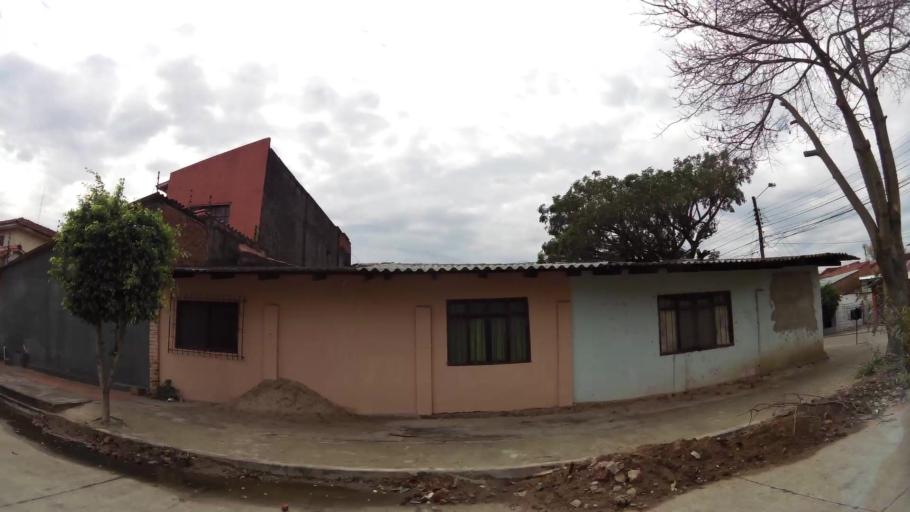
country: BO
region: Santa Cruz
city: Santa Cruz de la Sierra
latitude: -17.7487
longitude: -63.1930
